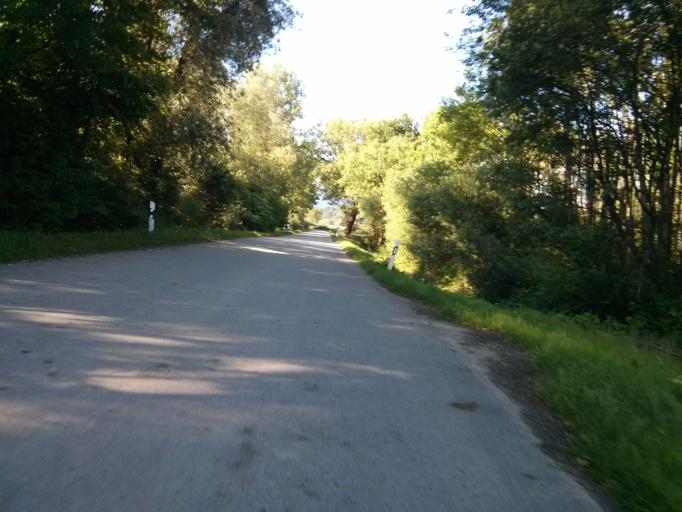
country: DE
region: Bavaria
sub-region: Lower Bavaria
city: Metten
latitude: 48.8343
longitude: 12.9085
